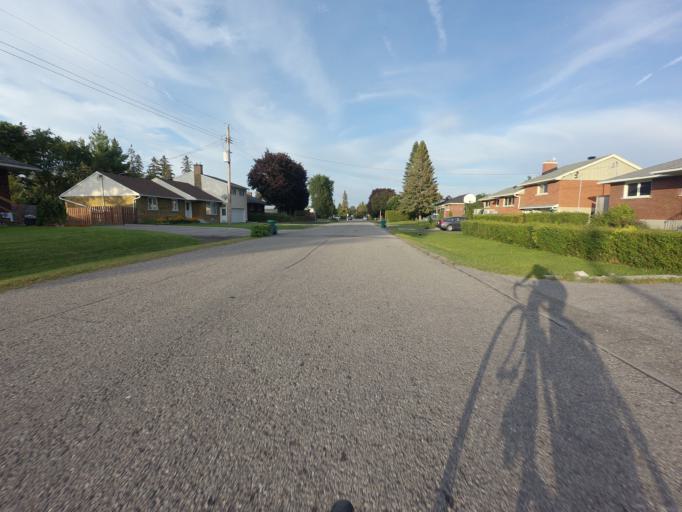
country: CA
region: Ontario
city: Bells Corners
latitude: 45.3415
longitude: -75.7537
